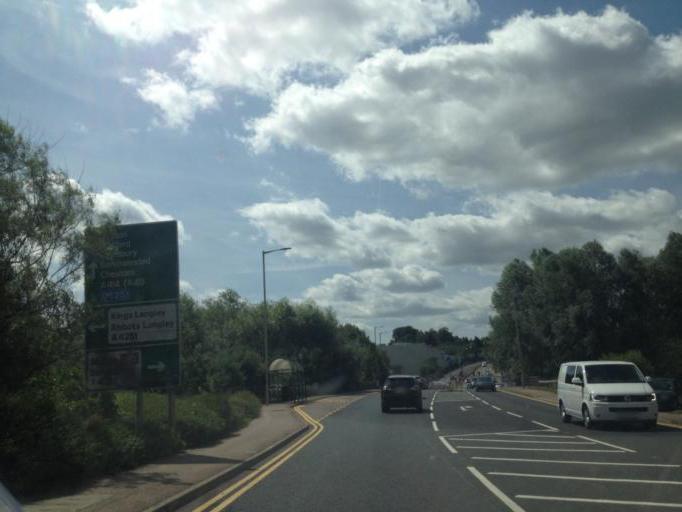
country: GB
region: England
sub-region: Hertfordshire
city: Hemel Hempstead
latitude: 51.7421
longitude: -0.4738
